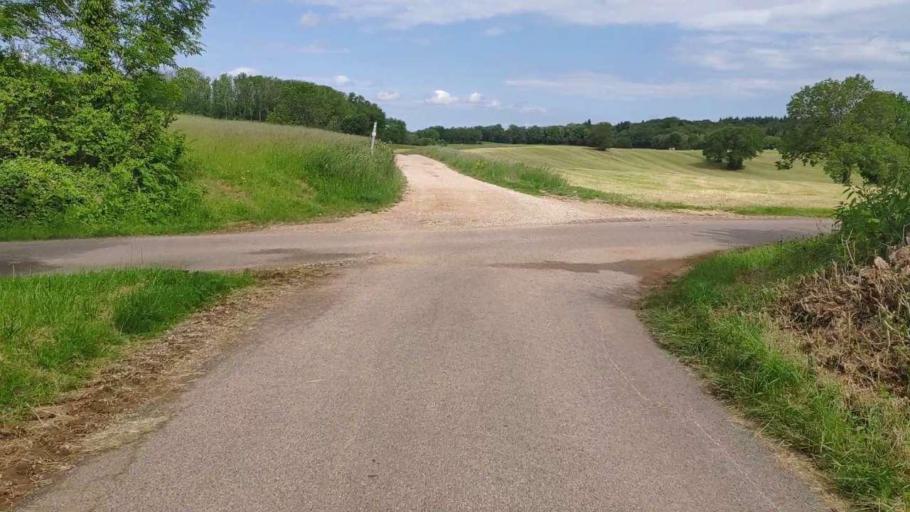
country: FR
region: Franche-Comte
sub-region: Departement du Jura
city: Poligny
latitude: 46.7761
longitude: 5.6288
